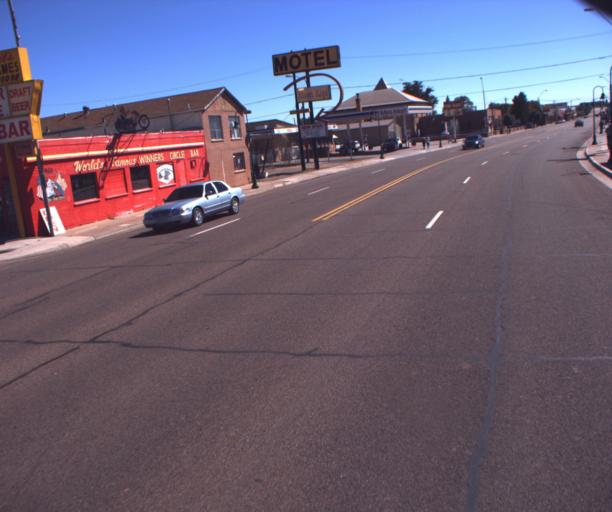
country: US
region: Arizona
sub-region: Navajo County
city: Holbrook
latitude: 34.9049
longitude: -110.1581
